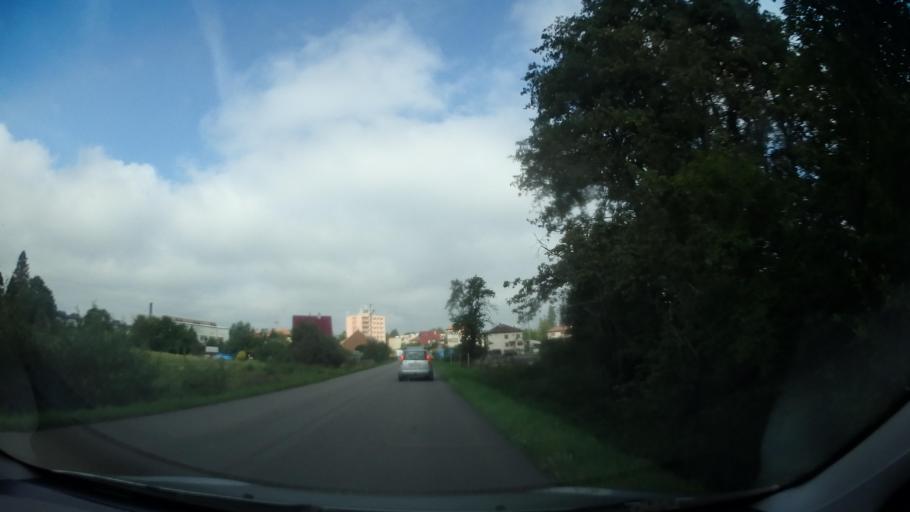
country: CZ
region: Central Bohemia
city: Neveklov
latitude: 49.7513
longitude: 14.5403
